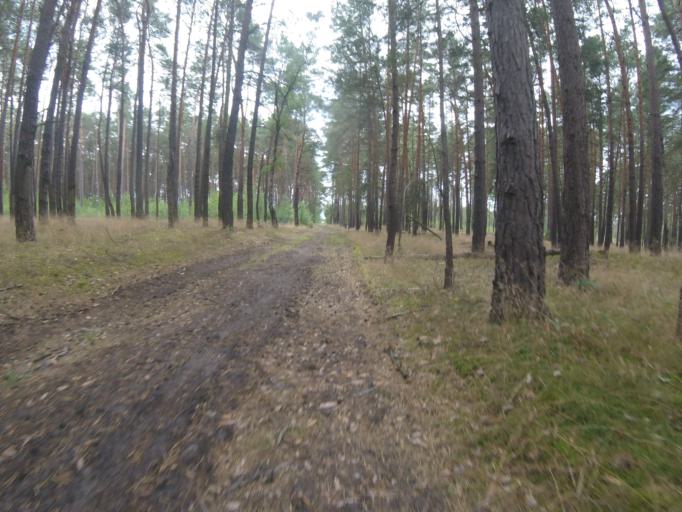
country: DE
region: Brandenburg
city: Bestensee
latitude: 52.2672
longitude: 13.7143
